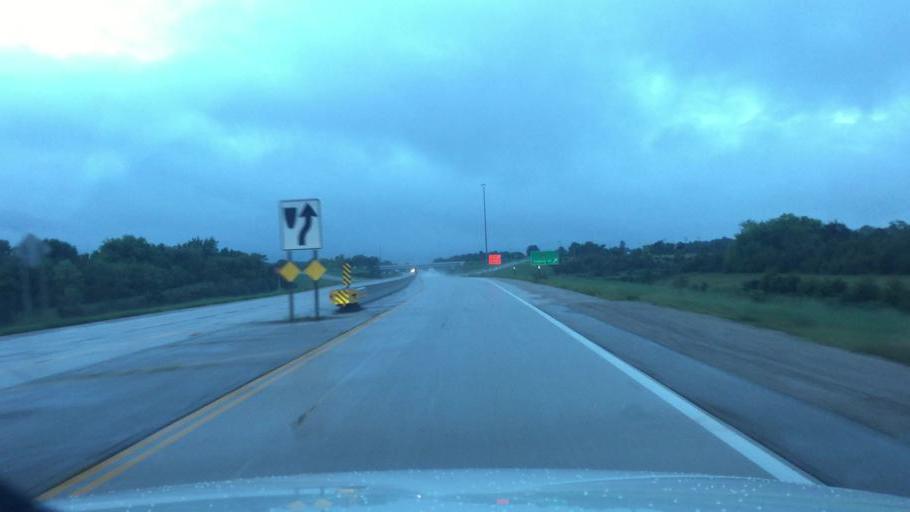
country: US
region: Kansas
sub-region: Neosho County
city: Chanute
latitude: 37.6947
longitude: -95.4795
